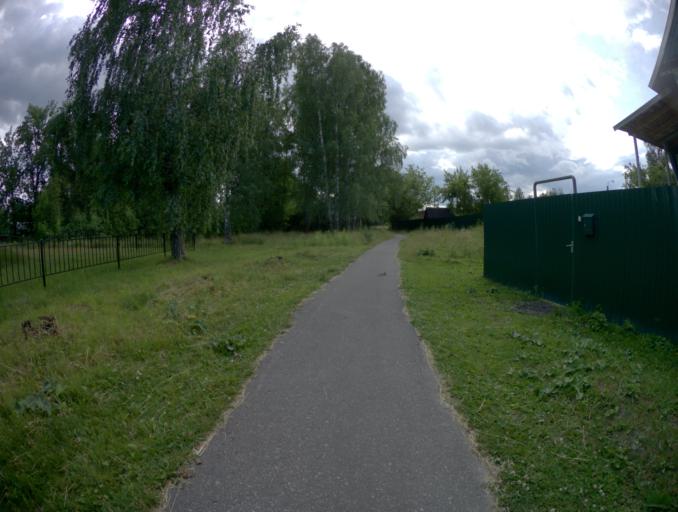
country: RU
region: Nizjnij Novgorod
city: Frolishchi
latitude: 56.4219
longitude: 42.6498
